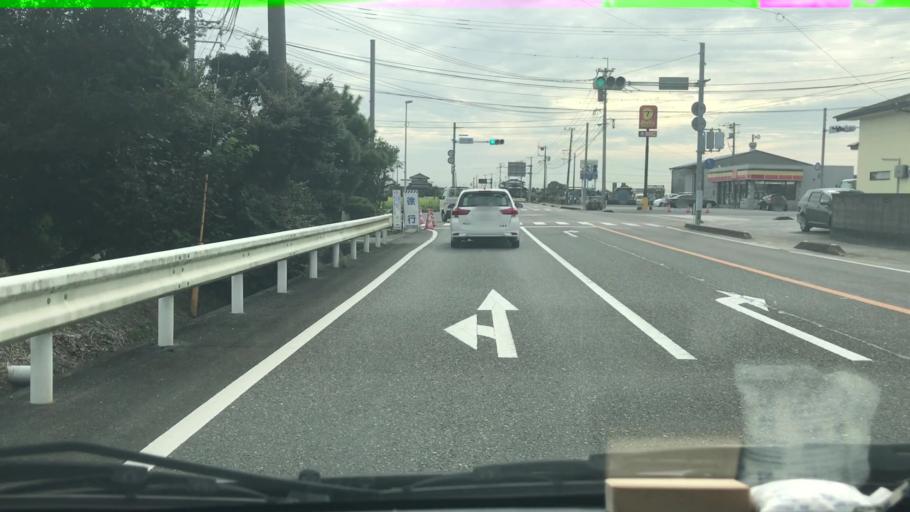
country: JP
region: Saga Prefecture
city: Takeocho-takeo
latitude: 33.1988
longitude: 130.1019
